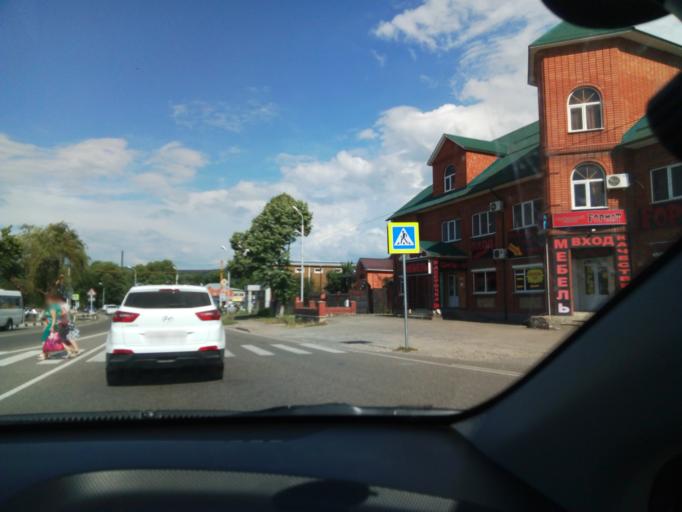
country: RU
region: Krasnodarskiy
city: Apsheronsk
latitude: 44.4653
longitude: 39.7272
